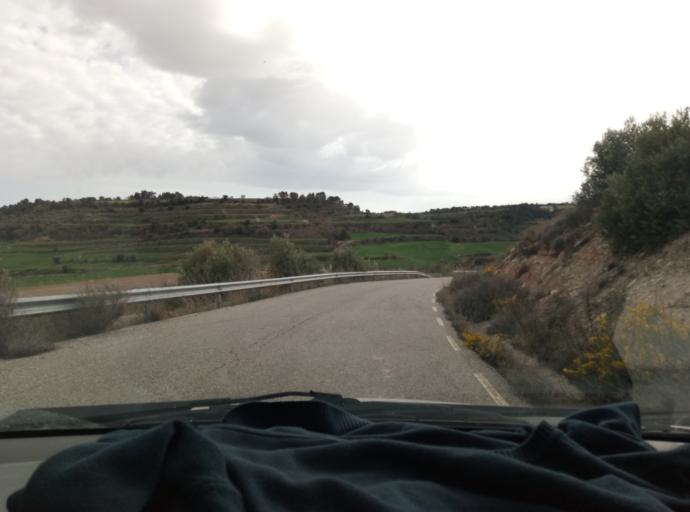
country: ES
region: Catalonia
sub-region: Provincia de Tarragona
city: Vallfogona de Riucorb
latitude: 41.6039
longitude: 1.2195
